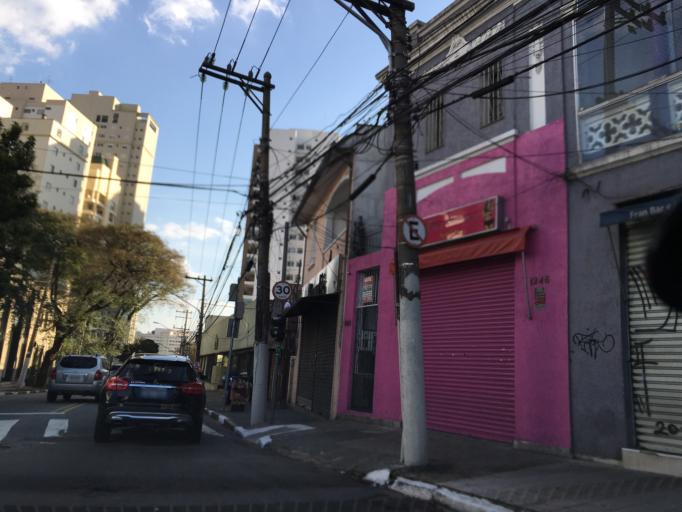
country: BR
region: Sao Paulo
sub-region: Sao Paulo
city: Sao Paulo
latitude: -23.5003
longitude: -46.6379
